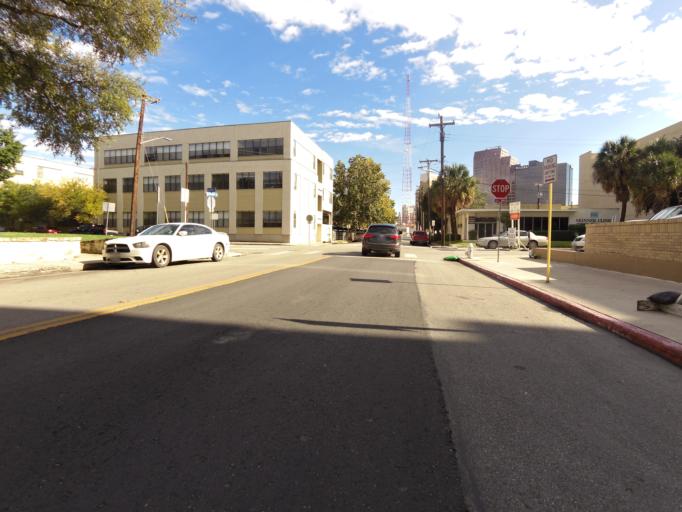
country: US
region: Texas
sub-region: Bexar County
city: San Antonio
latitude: 29.4337
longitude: -98.4919
